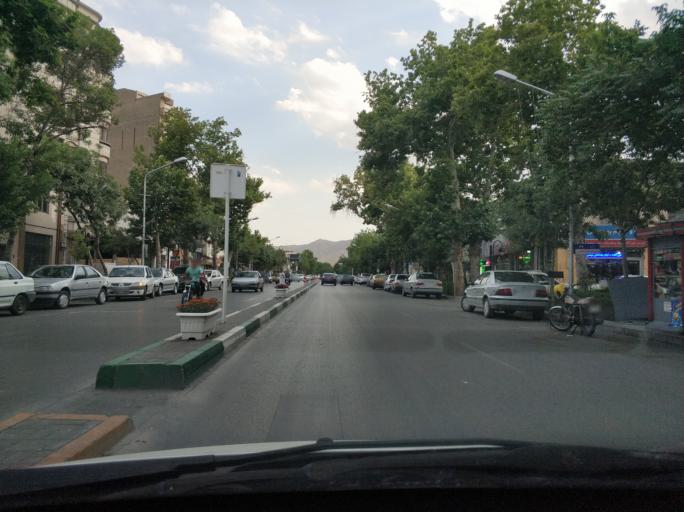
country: IR
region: Razavi Khorasan
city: Mashhad
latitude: 36.2826
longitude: 59.5966
